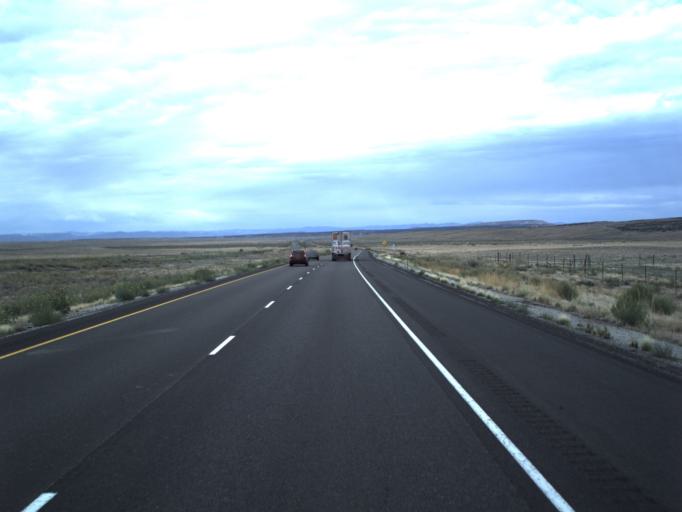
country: US
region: Colorado
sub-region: Mesa County
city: Loma
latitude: 39.0628
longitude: -109.2501
